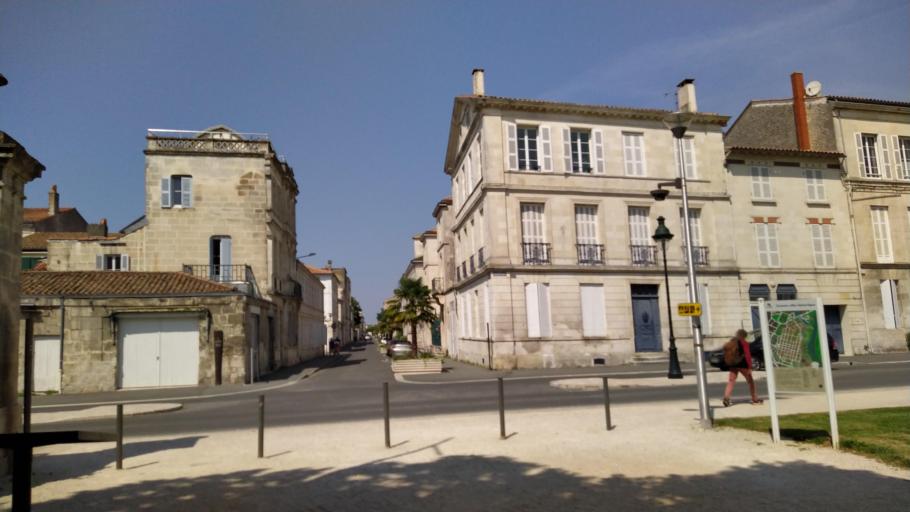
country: FR
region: Poitou-Charentes
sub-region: Departement de la Charente-Maritime
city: Rochefort
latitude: 45.9384
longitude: -0.9579
